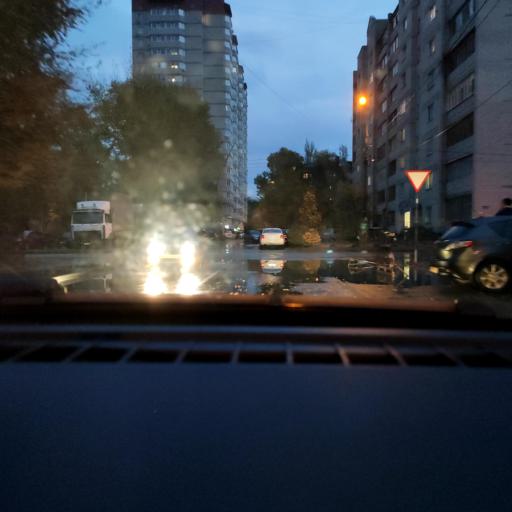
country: RU
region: Voronezj
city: Maslovka
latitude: 51.6174
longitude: 39.2453
